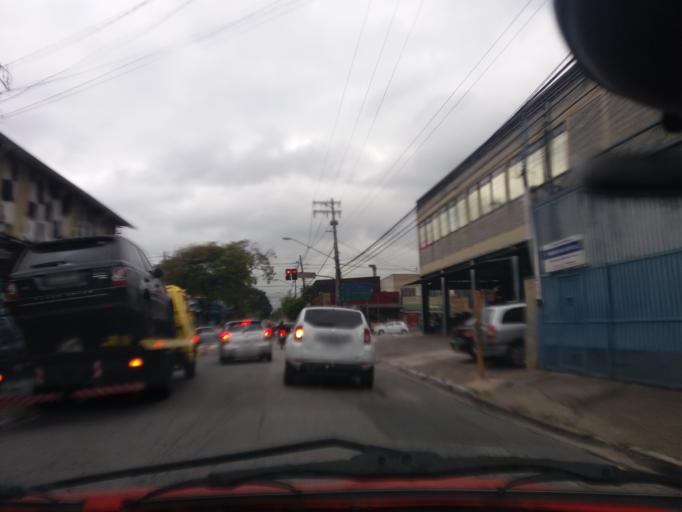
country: BR
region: Sao Paulo
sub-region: Taboao Da Serra
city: Taboao da Serra
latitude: -23.5888
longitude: -46.7367
